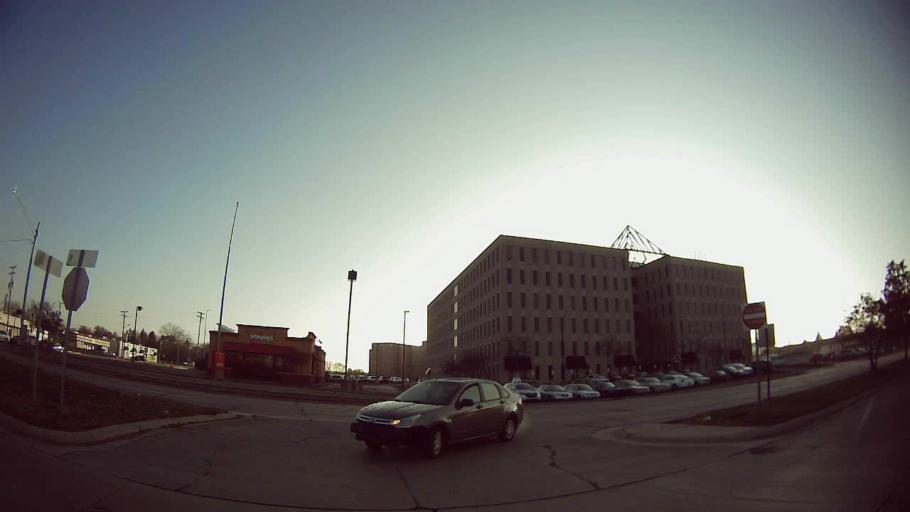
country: US
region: Michigan
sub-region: Oakland County
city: Southfield
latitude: 42.4807
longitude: -83.2022
